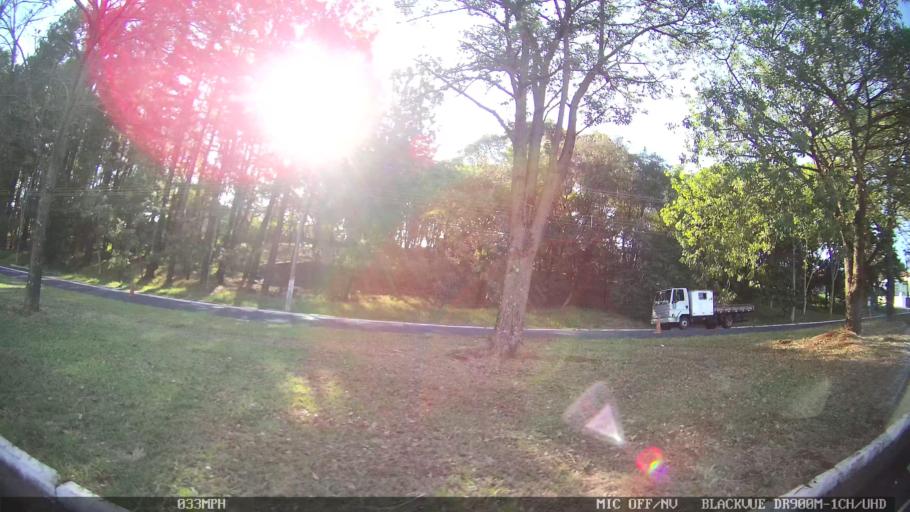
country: BR
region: Sao Paulo
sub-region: Ribeirao Preto
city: Ribeirao Preto
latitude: -21.2051
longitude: -47.7838
